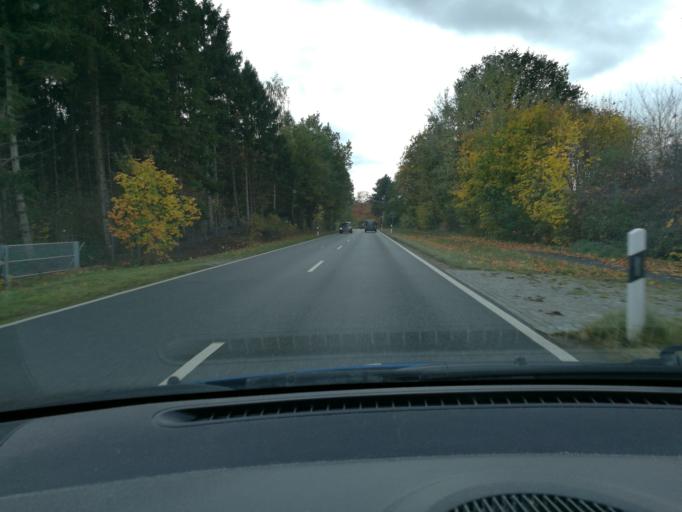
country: DE
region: Schleswig-Holstein
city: Gross Sarau
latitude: 53.7624
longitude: 10.7309
